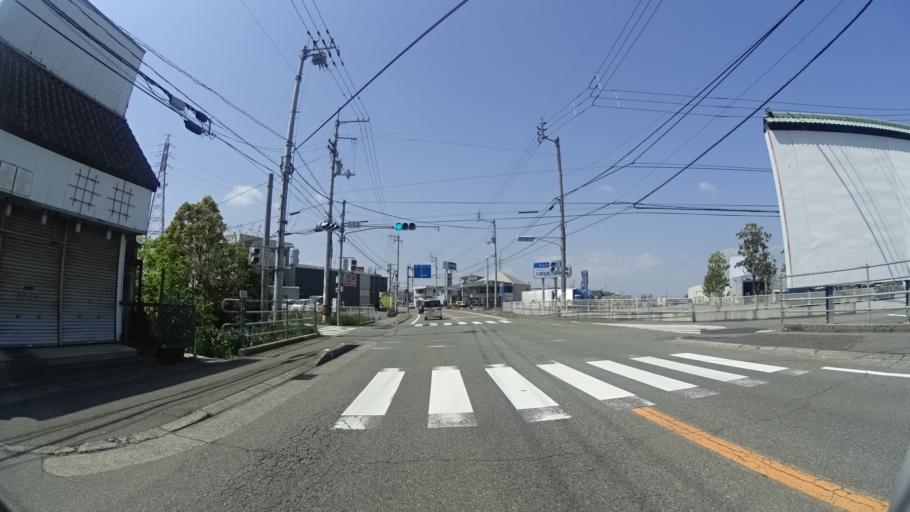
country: JP
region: Tokushima
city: Narutocho-mitsuishi
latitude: 34.1621
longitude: 134.5939
